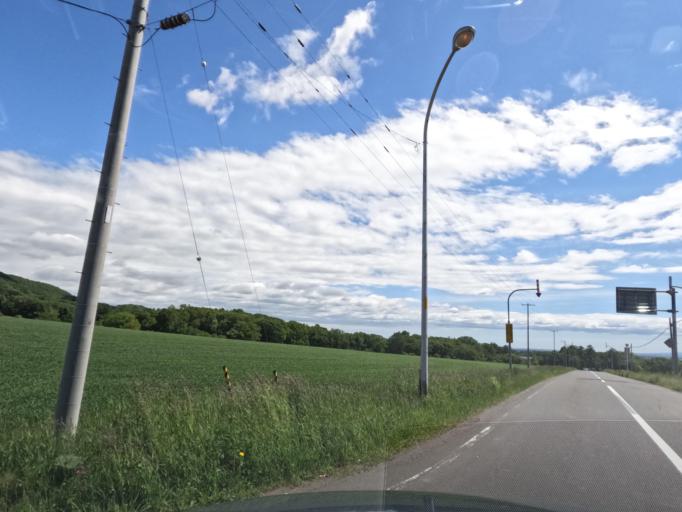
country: JP
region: Hokkaido
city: Kitahiroshima
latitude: 42.9965
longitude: 141.7295
